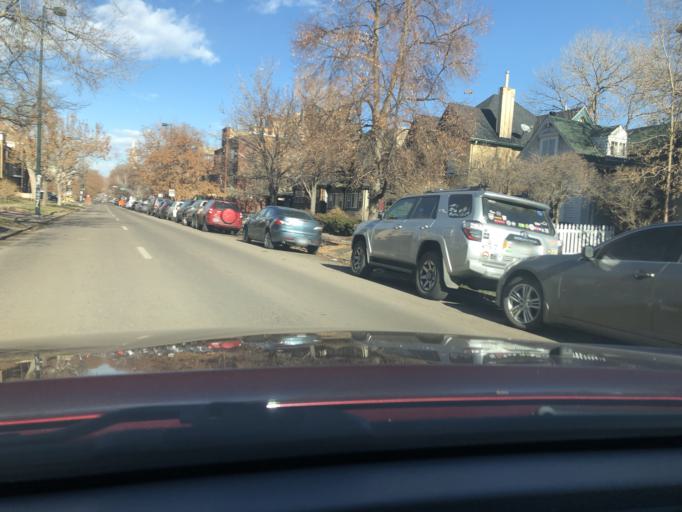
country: US
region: Colorado
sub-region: Denver County
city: Denver
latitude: 39.7352
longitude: -104.9823
